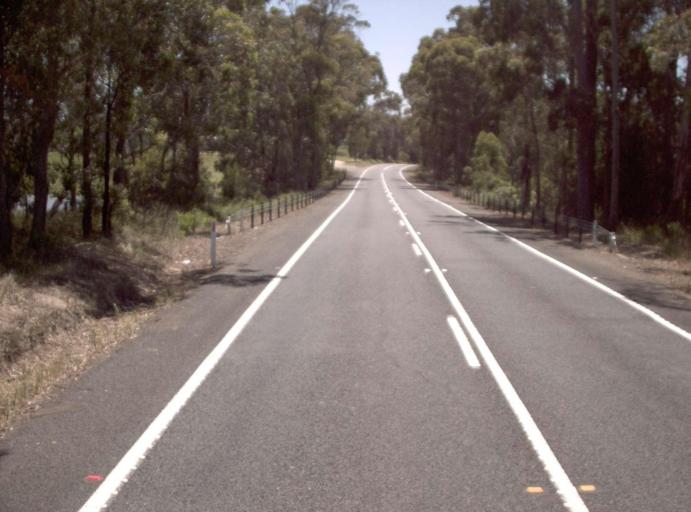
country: AU
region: Victoria
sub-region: East Gippsland
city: Lakes Entrance
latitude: -37.8348
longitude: 148.0315
